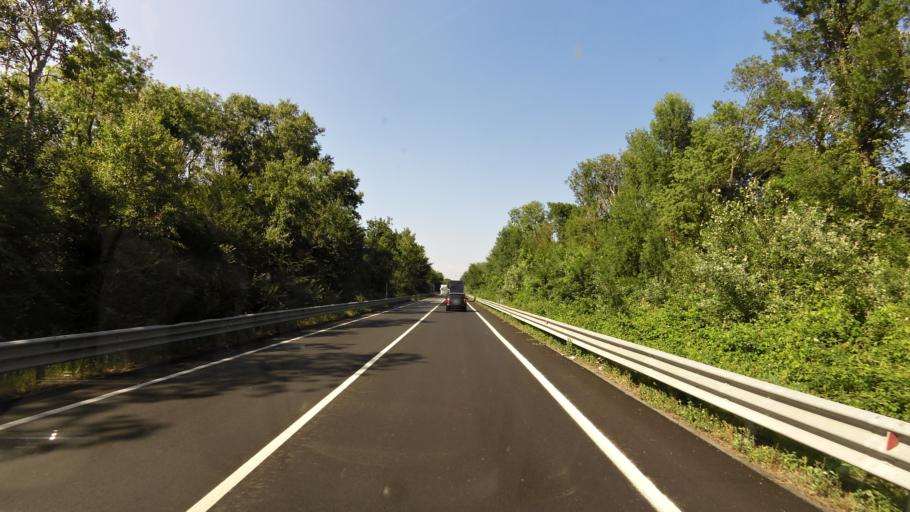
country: IT
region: Emilia-Romagna
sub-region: Provincia di Ravenna
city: Marina Romea
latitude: 44.5187
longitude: 12.2274
